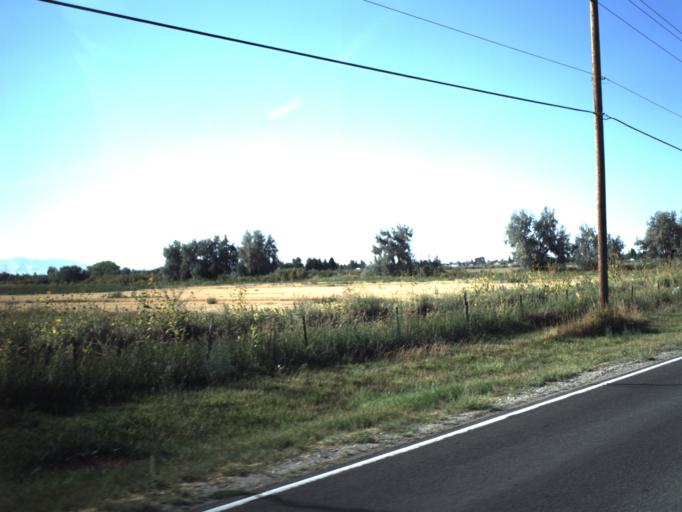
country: US
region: Utah
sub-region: Weber County
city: Hooper
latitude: 41.1438
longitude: -112.1229
